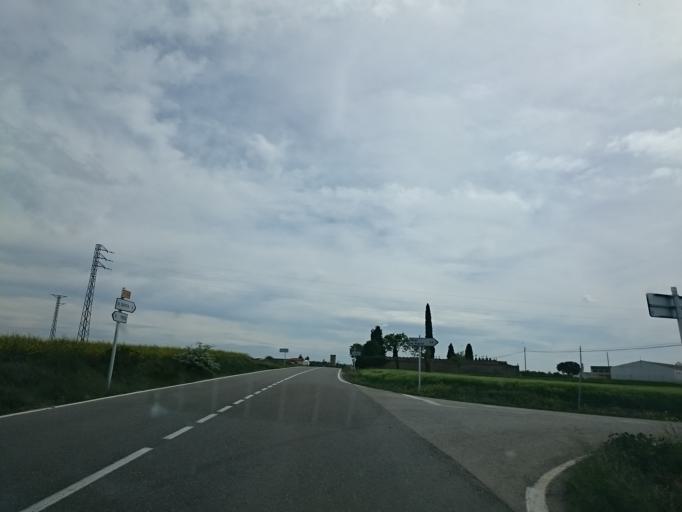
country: ES
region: Catalonia
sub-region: Provincia de Lleida
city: Ivorra
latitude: 41.7463
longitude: 1.3852
